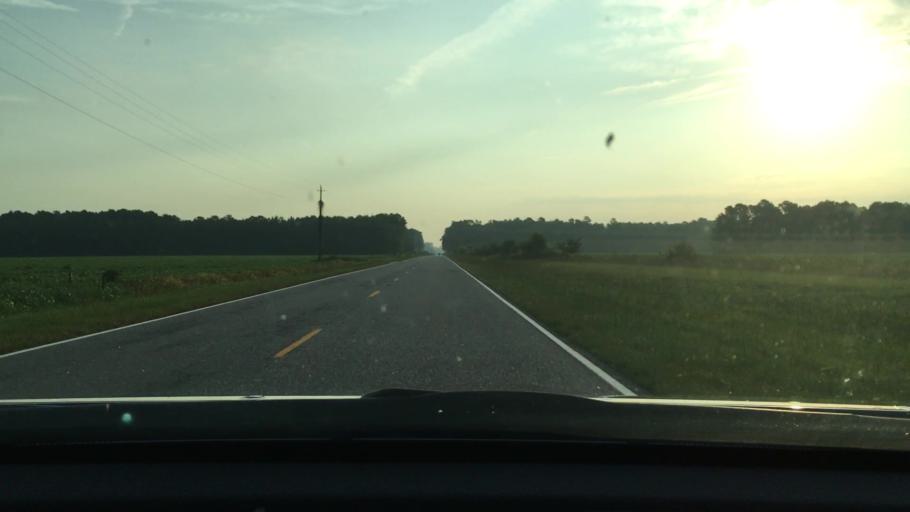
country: US
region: South Carolina
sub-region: Lee County
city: Bishopville
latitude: 34.0835
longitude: -80.1932
